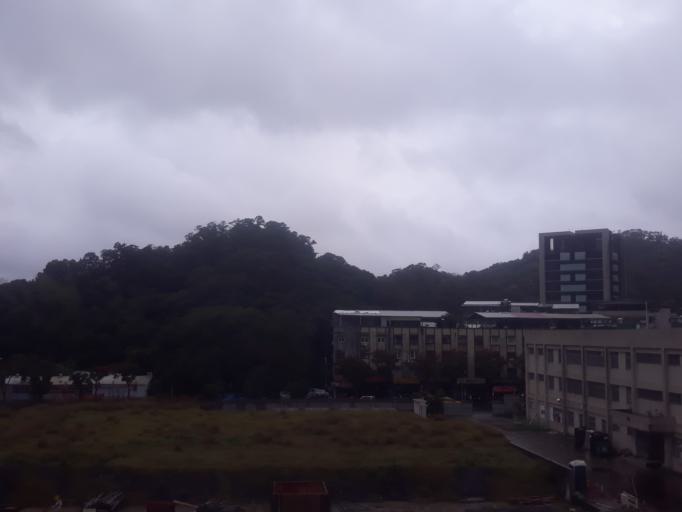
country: TW
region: Taipei
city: Taipei
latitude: 25.0025
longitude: 121.5570
